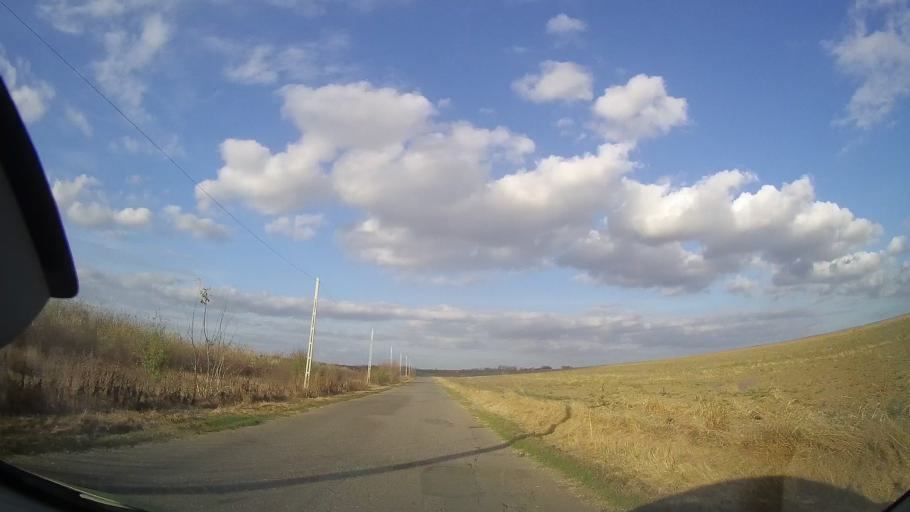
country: RO
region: Constanta
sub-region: Comuna Cerchezu
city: Cerchezu
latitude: 43.8470
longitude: 28.0989
